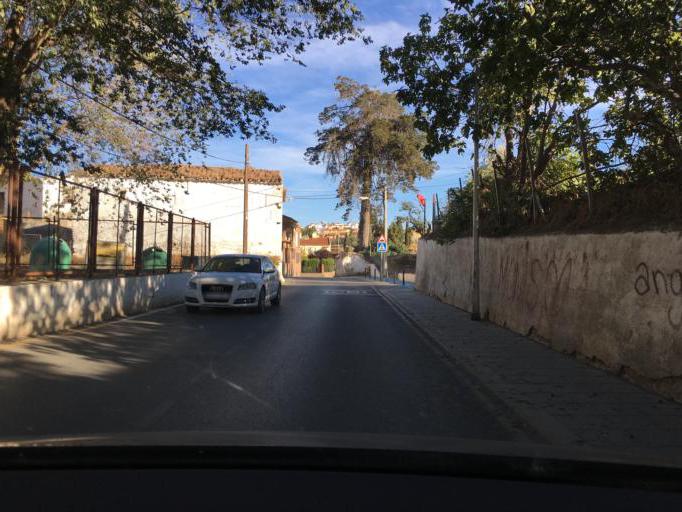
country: ES
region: Andalusia
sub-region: Provincia de Granada
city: Guadix
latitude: 37.2962
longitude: -3.1318
